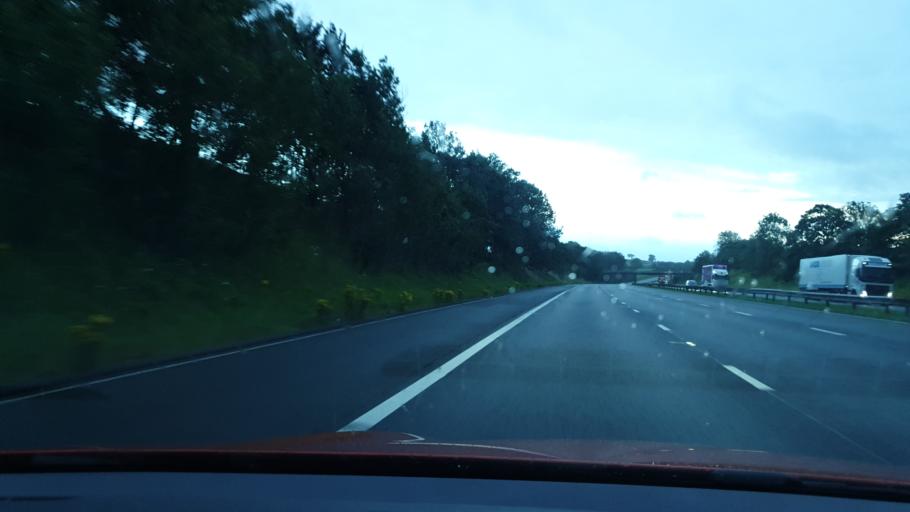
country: GB
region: England
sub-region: Cumbria
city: Milnthorpe
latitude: 54.1962
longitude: -2.7236
